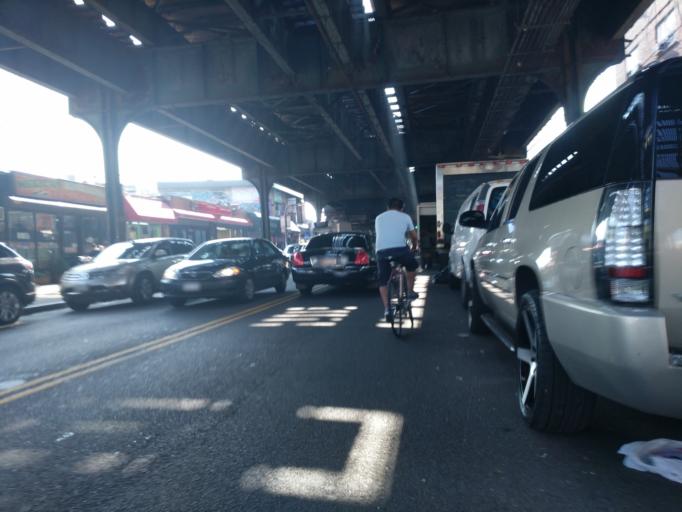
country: US
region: New York
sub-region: Queens County
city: Borough of Queens
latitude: 40.7494
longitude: -73.8684
